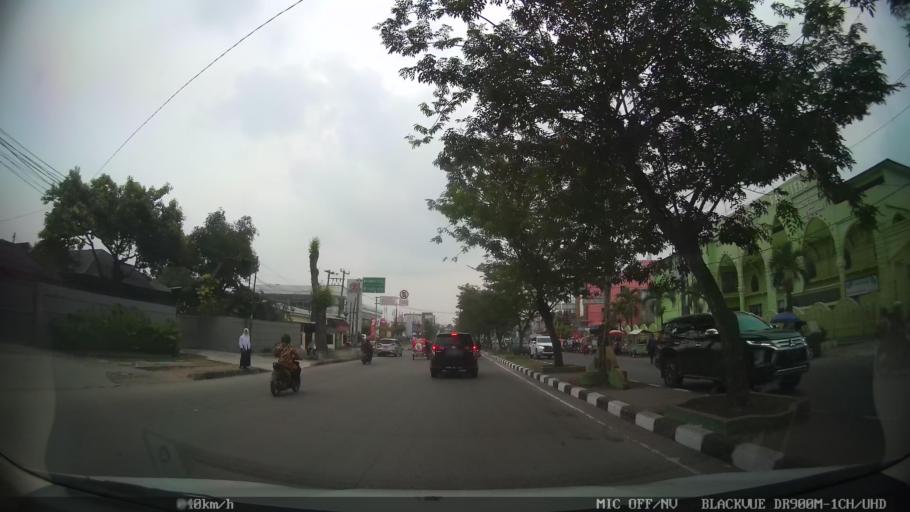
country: ID
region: North Sumatra
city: Deli Tua
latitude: 3.5445
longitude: 98.6986
